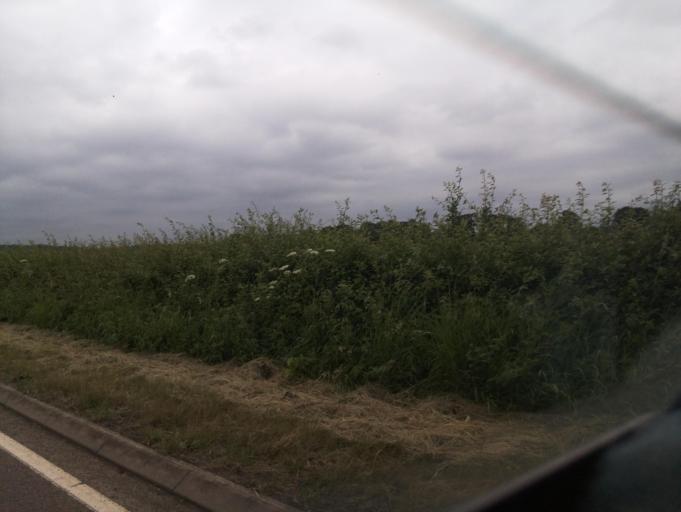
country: GB
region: England
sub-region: Leicestershire
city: Melton Mowbray
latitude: 52.7331
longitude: -0.8492
